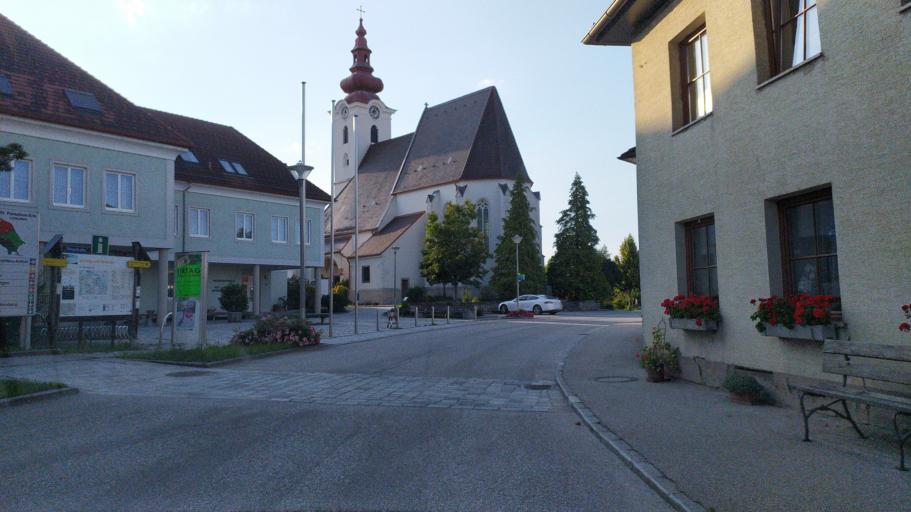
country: AT
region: Lower Austria
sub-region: Politischer Bezirk Amstetten
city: Ennsdorf
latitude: 48.2107
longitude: 14.5687
